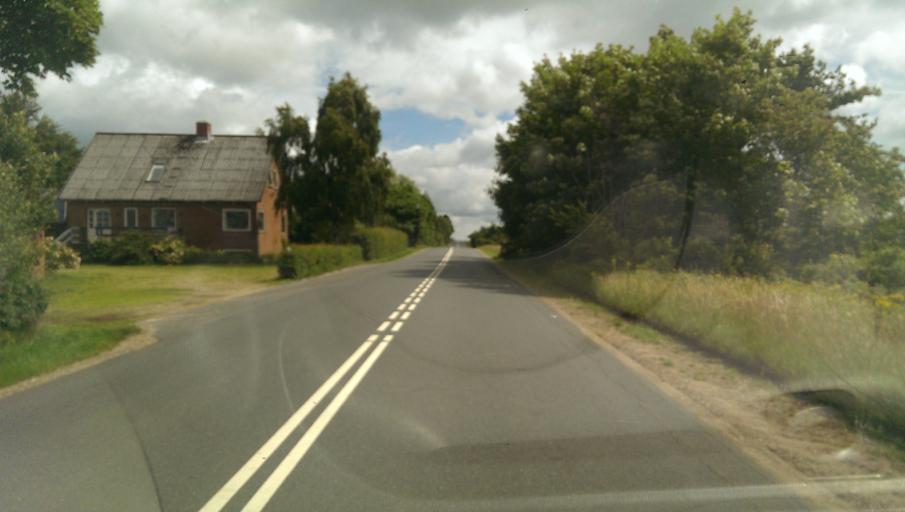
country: DK
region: Central Jutland
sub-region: Silkeborg Kommune
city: Virklund
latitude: 56.0914
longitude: 9.4921
